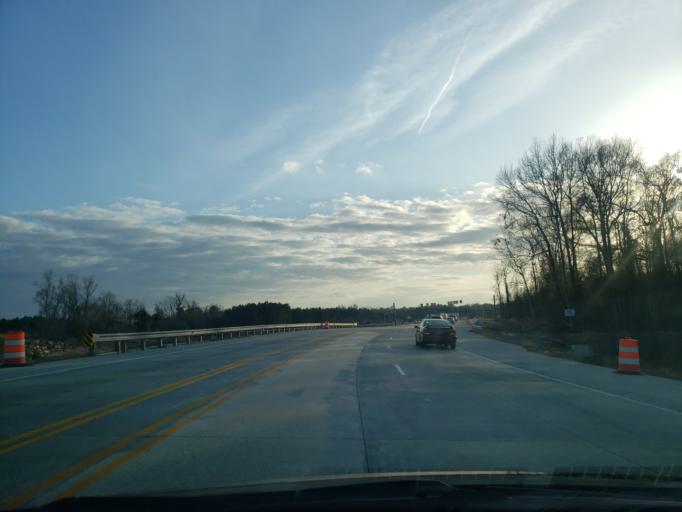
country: US
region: Georgia
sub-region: Chatham County
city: Bloomingdale
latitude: 32.1382
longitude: -81.3092
